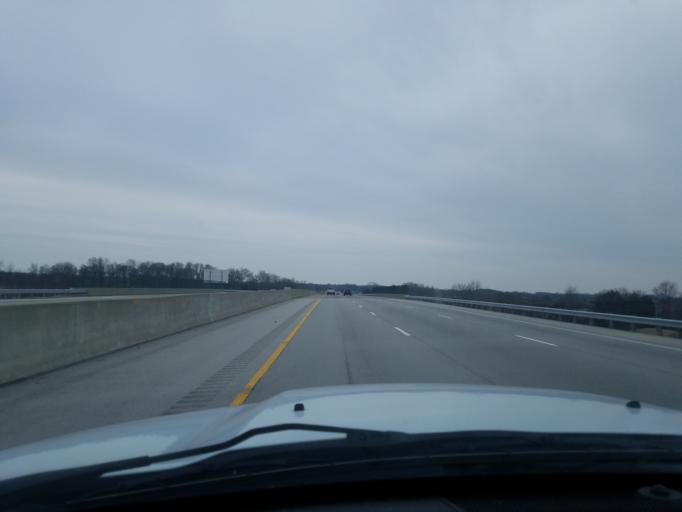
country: US
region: Kentucky
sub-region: Barren County
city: Cave City
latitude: 37.0906
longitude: -86.0607
